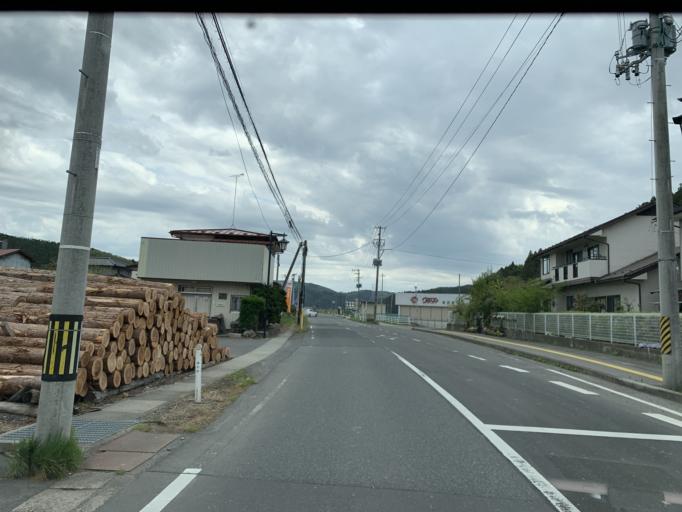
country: JP
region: Iwate
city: Ichinoseki
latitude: 38.7667
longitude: 141.3277
